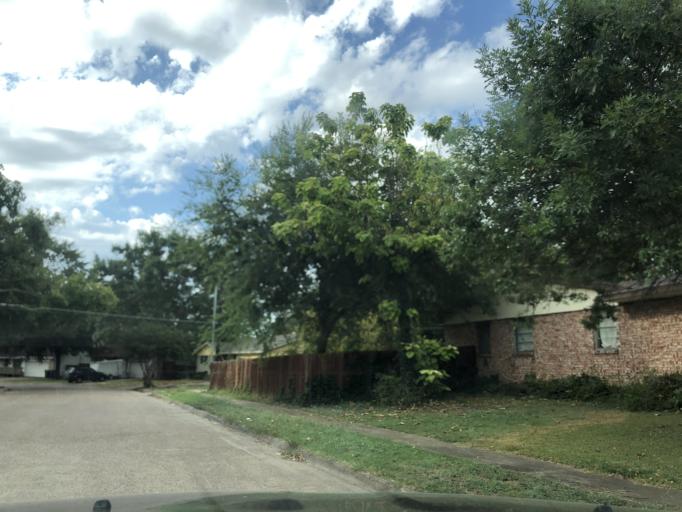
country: US
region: Texas
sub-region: Dallas County
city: Garland
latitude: 32.8881
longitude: -96.6627
